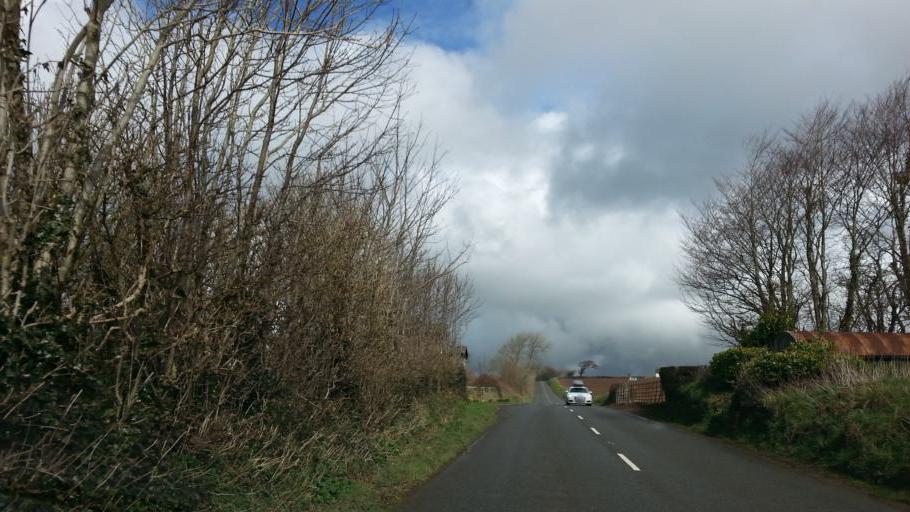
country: GB
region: England
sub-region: Devon
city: Barnstaple
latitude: 51.1179
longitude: -4.0144
